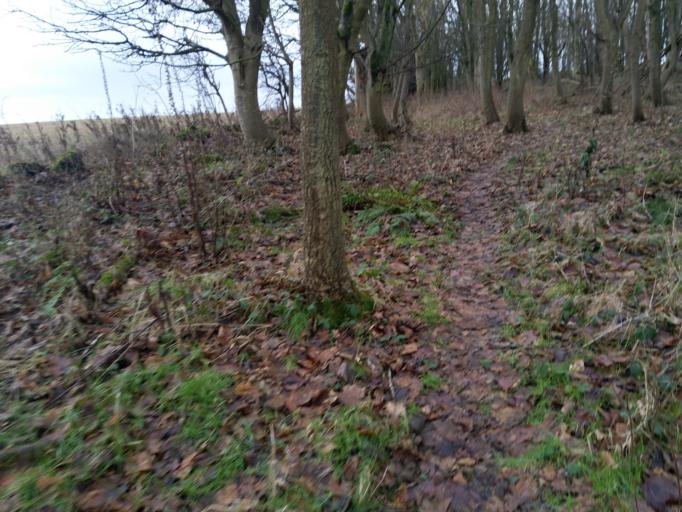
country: GB
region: Scotland
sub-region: Fife
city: Limekilns
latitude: 55.9944
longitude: -3.5115
